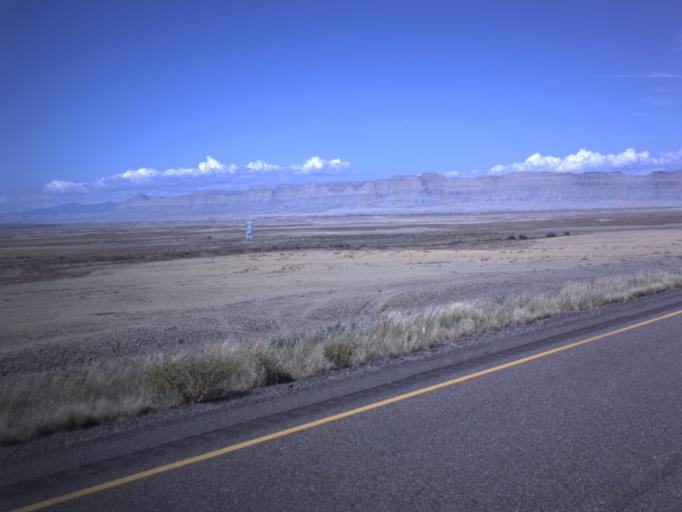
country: US
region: Utah
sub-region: Carbon County
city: East Carbon City
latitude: 38.9456
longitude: -110.3247
